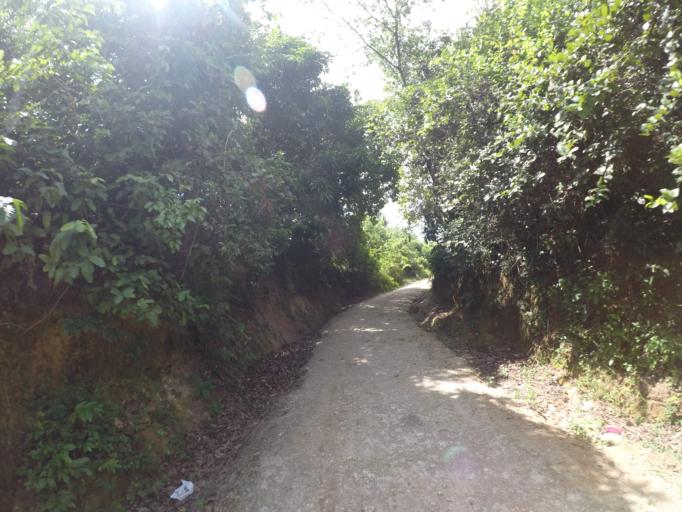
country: TZ
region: Pemba South
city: Mtambile
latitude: -5.3871
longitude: 39.7415
